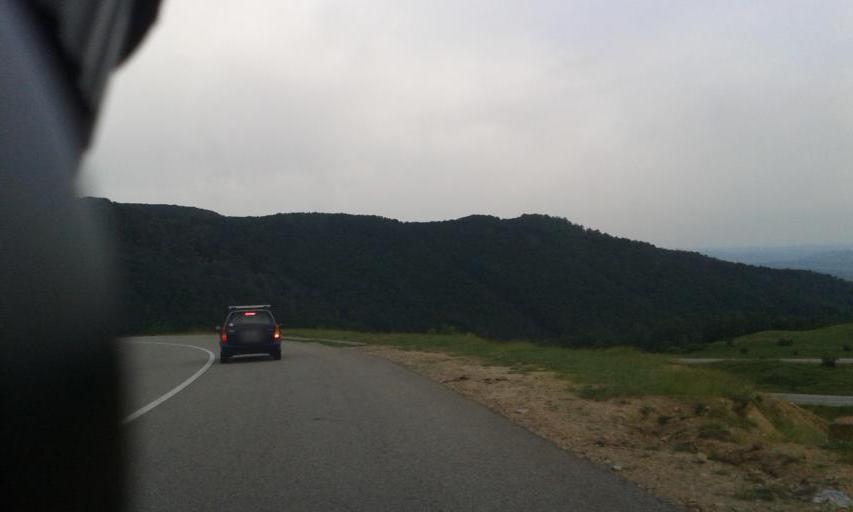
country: RO
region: Gorj
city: Novaci-Straini
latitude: 45.2199
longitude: 23.6971
